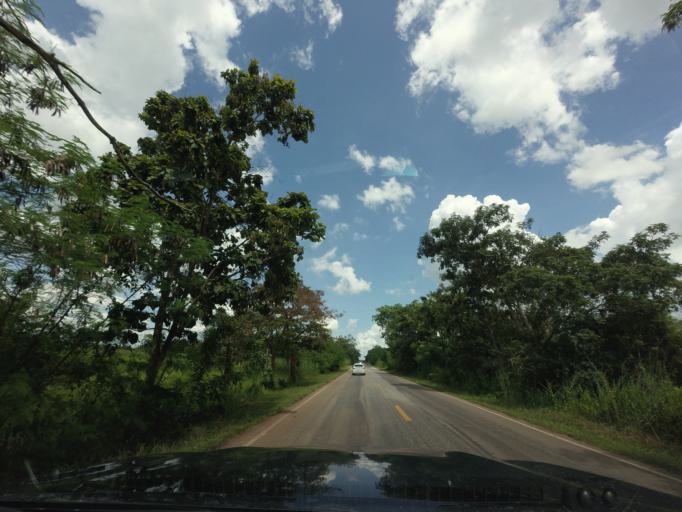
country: TH
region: Changwat Udon Thani
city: Ban Dung
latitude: 17.6809
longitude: 103.1885
